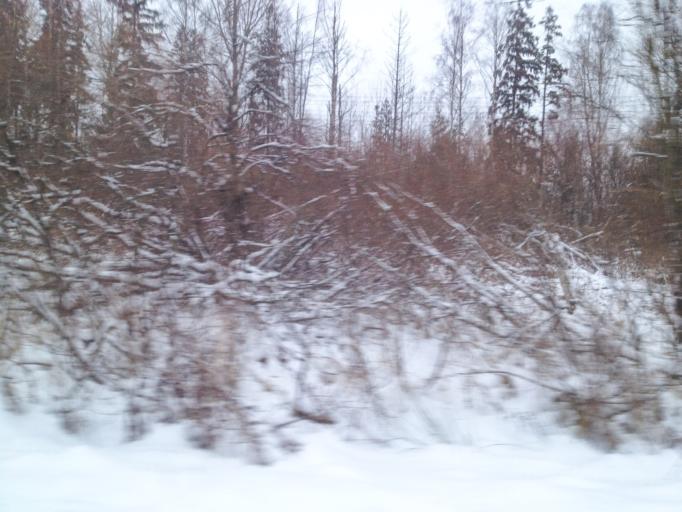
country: FI
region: Uusimaa
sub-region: Helsinki
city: Vantaa
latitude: 60.2198
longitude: 25.1559
